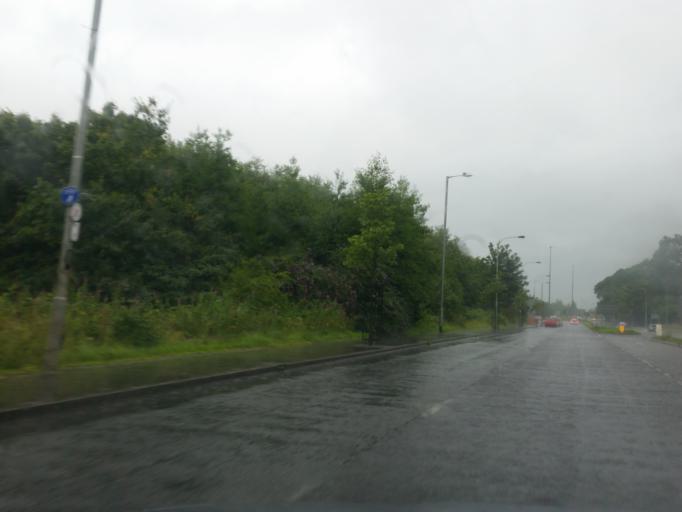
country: GB
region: Northern Ireland
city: Holywood
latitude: 54.6155
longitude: -5.8615
